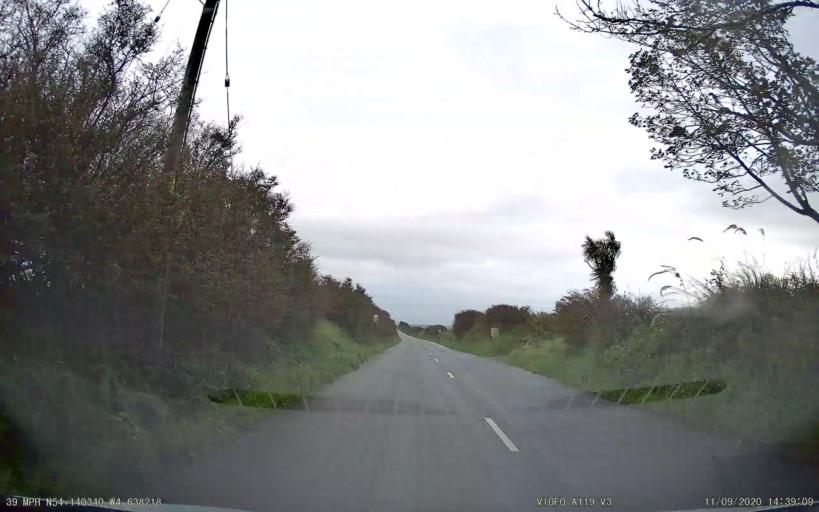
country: IM
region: Castletown
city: Castletown
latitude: 54.1403
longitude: -4.6382
